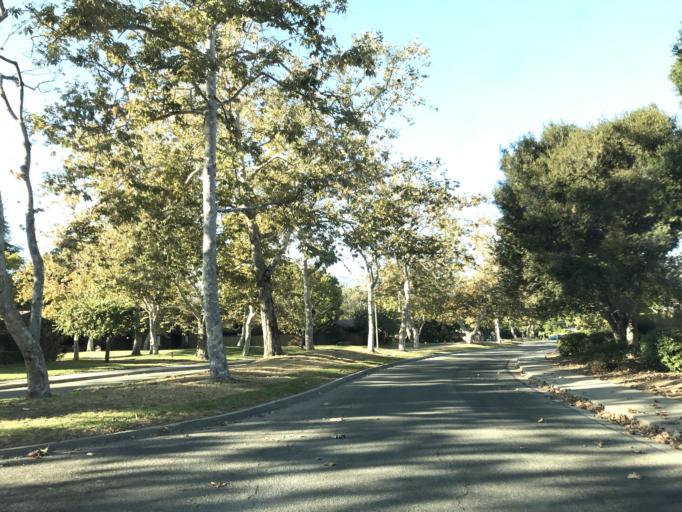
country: US
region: California
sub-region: Santa Barbara County
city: Goleta
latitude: 34.4516
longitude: -119.8116
